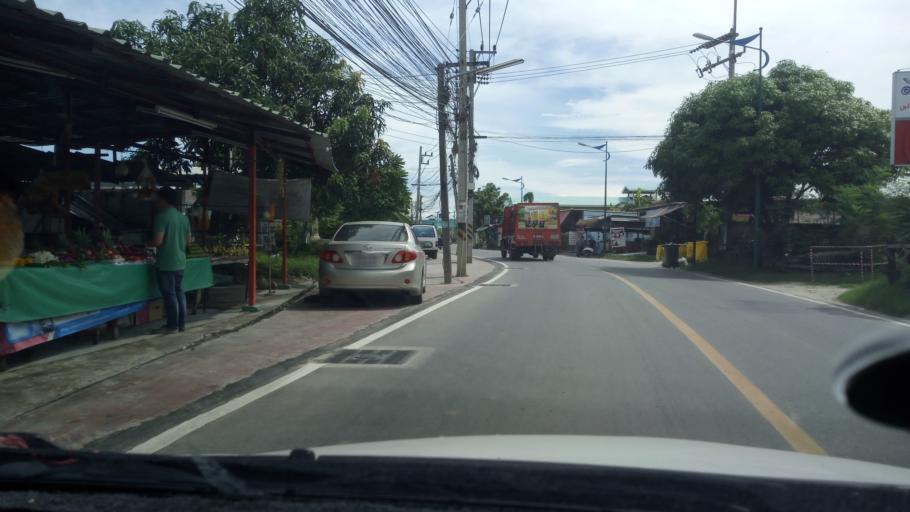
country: TH
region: Chon Buri
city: Chon Buri
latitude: 13.4204
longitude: 101.0334
